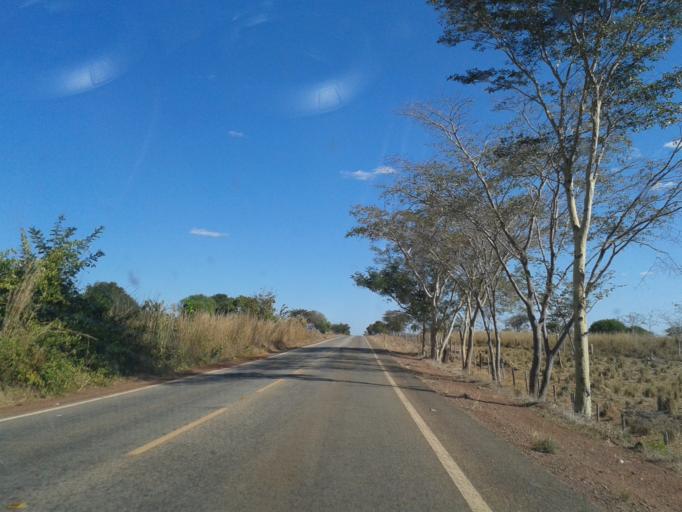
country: BR
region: Goias
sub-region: Mozarlandia
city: Mozarlandia
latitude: -14.5605
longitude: -50.4971
